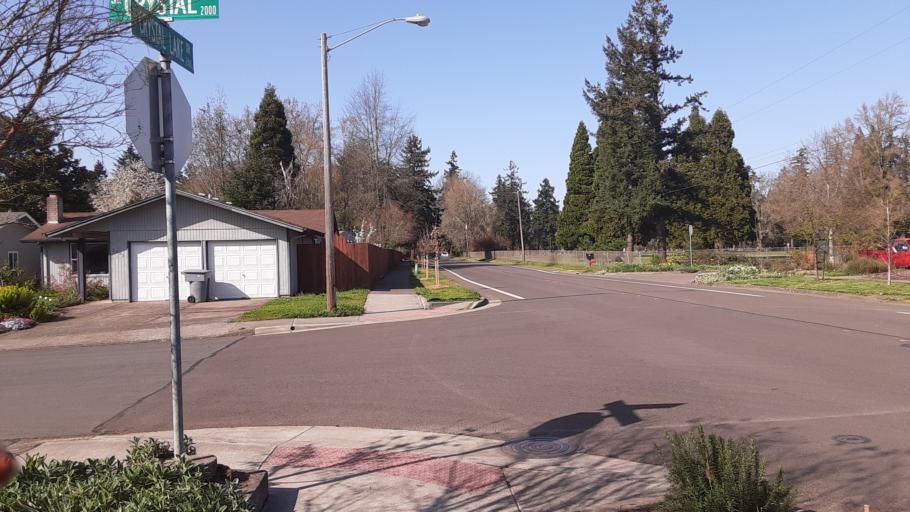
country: US
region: Oregon
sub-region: Benton County
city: Corvallis
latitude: 44.5461
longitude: -123.2558
